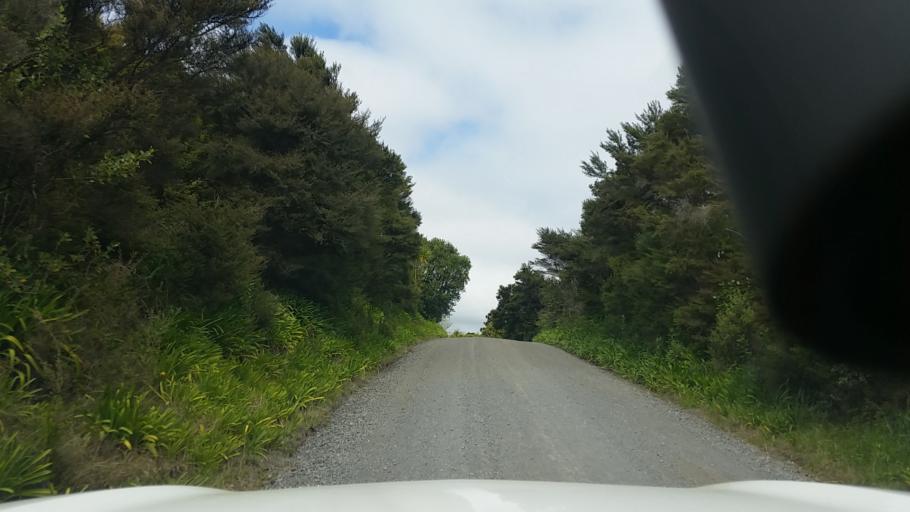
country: NZ
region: Auckland
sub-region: Auckland
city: Muriwai Beach
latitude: -36.8436
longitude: 174.5117
